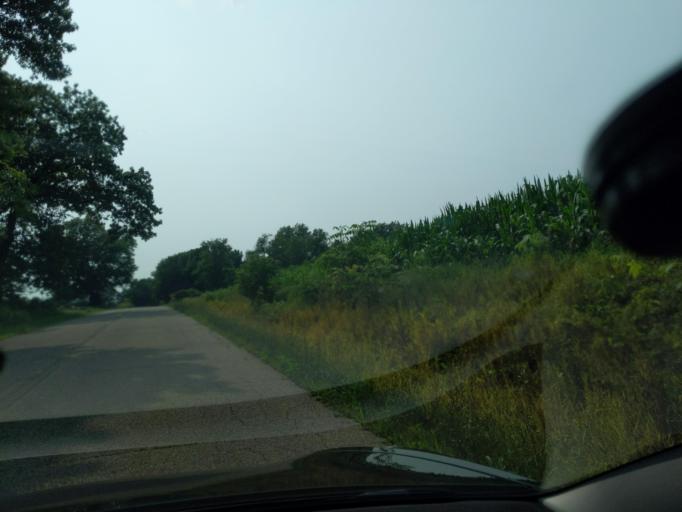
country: US
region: Michigan
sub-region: Eaton County
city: Eaton Rapids
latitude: 42.4220
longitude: -84.5770
